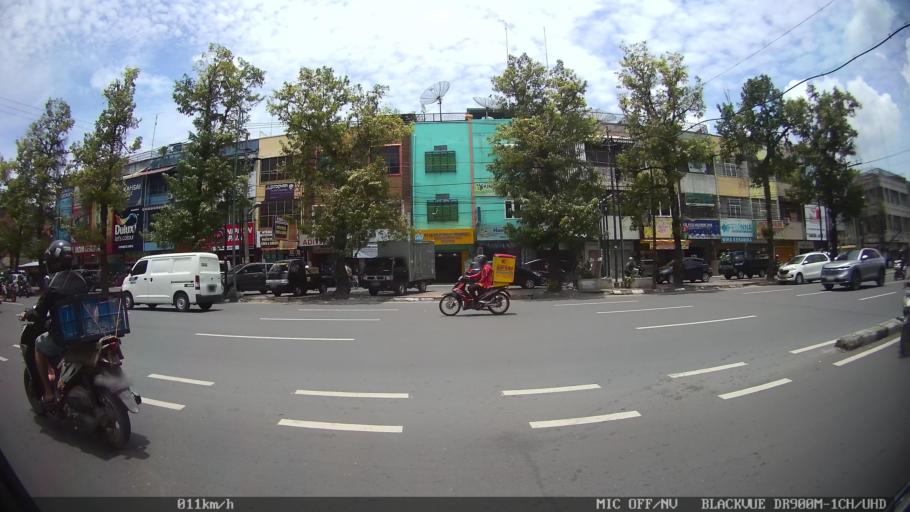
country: ID
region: North Sumatra
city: Medan
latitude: 3.5924
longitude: 98.6664
